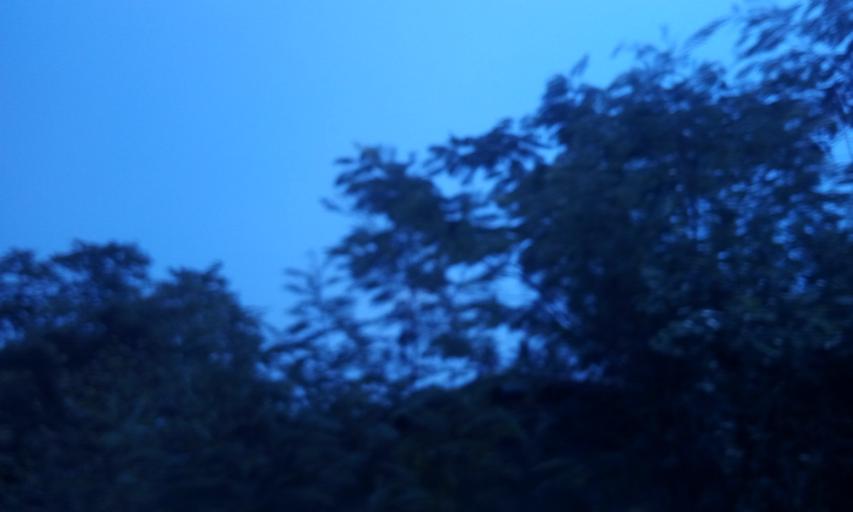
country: TH
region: Chachoengsao
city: Bang Nam Priao
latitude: 13.9293
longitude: 100.9769
